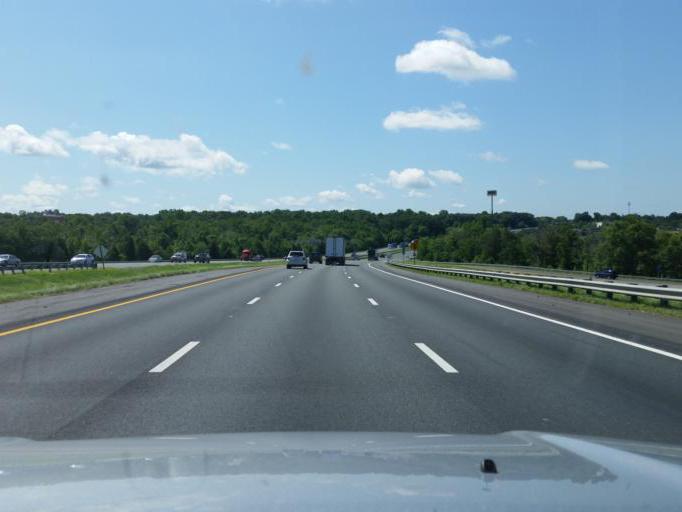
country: US
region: Virginia
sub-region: City of Fredericksburg
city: Fredericksburg
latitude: 38.2383
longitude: -77.4993
